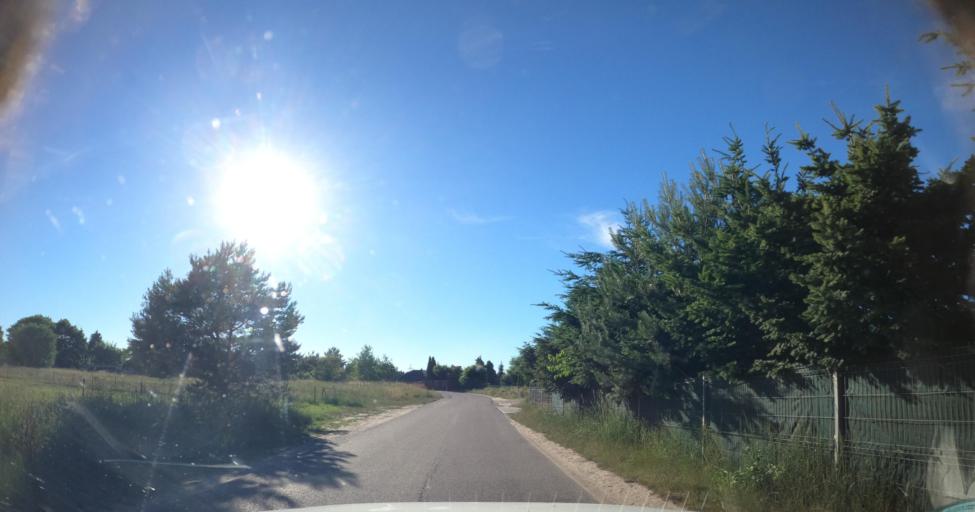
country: PL
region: West Pomeranian Voivodeship
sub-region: Szczecin
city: Szczecin
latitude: 53.4826
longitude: 14.5258
